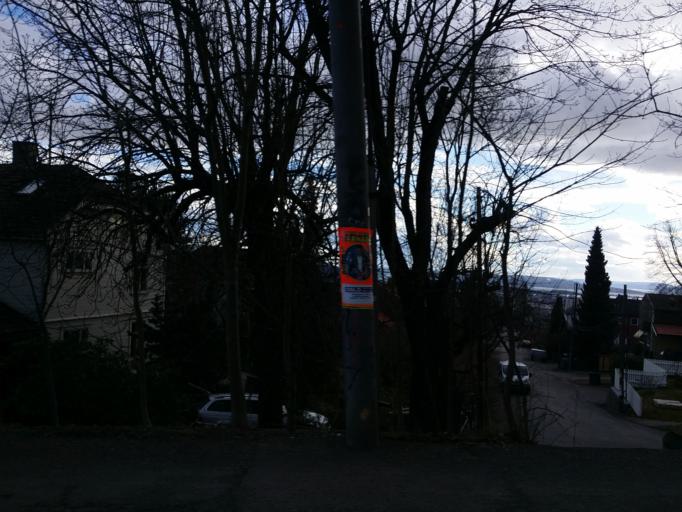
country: NO
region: Oslo
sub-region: Oslo
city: Oslo
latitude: 59.9509
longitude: 10.7871
